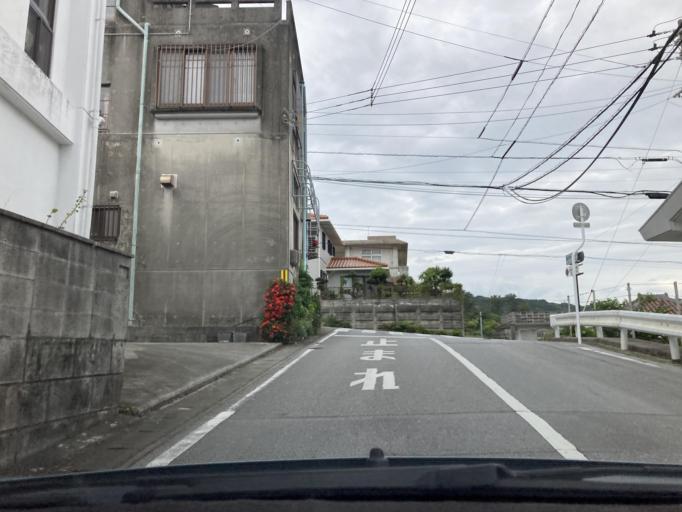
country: JP
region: Okinawa
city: Tomigusuku
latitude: 26.1702
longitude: 127.7725
